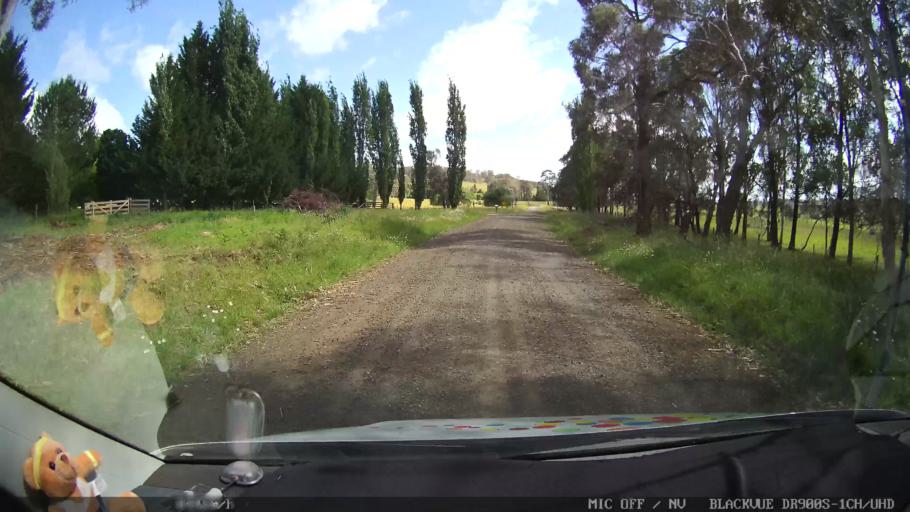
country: AU
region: New South Wales
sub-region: Glen Innes Severn
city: Glen Innes
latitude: -29.9645
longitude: 151.6993
